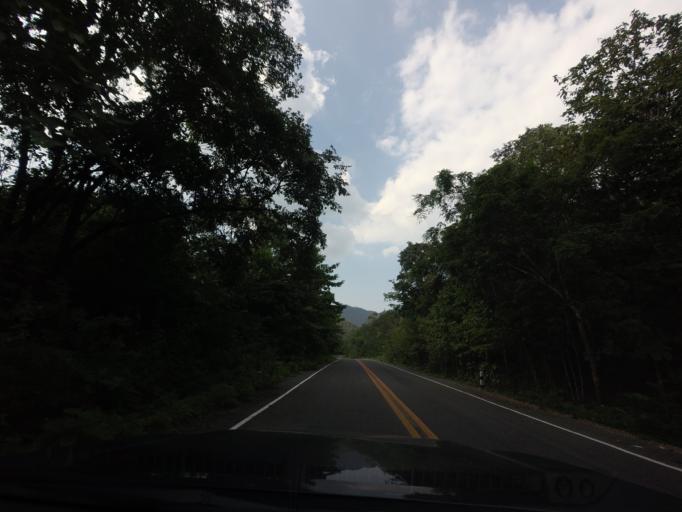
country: TH
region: Nan
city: Na Noi
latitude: 18.2958
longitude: 100.9022
